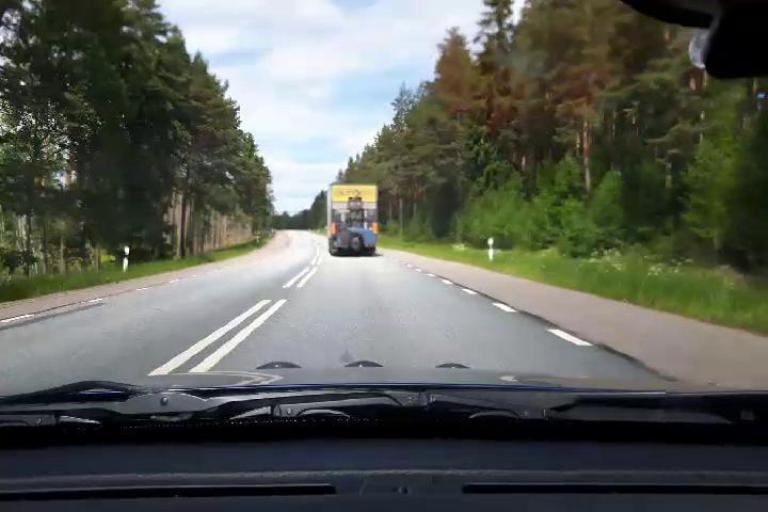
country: SE
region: Uppsala
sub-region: Tierps Kommun
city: Tierp
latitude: 60.2056
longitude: 17.4825
